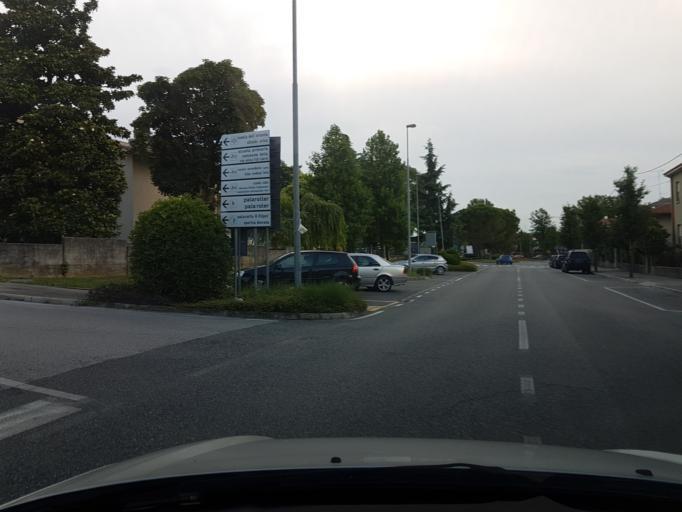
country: IT
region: Friuli Venezia Giulia
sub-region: Provincia di Gorizia
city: Ronchi dei Legionari
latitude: 45.8251
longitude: 13.5054
